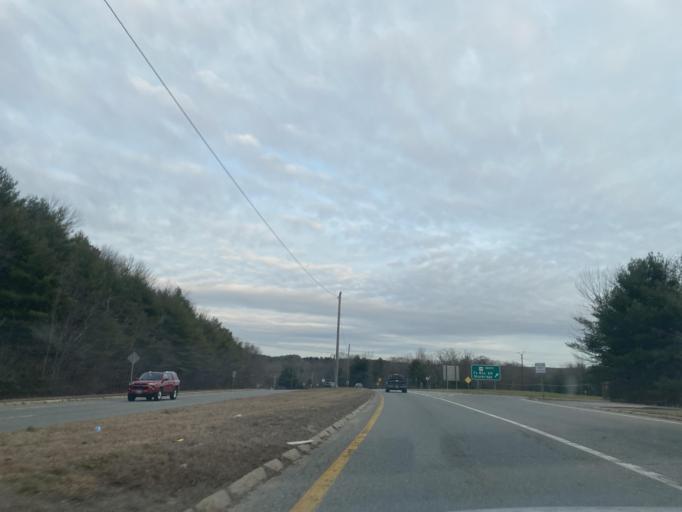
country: US
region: Massachusetts
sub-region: Worcester County
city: East Brookfield
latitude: 42.2314
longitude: -72.0208
